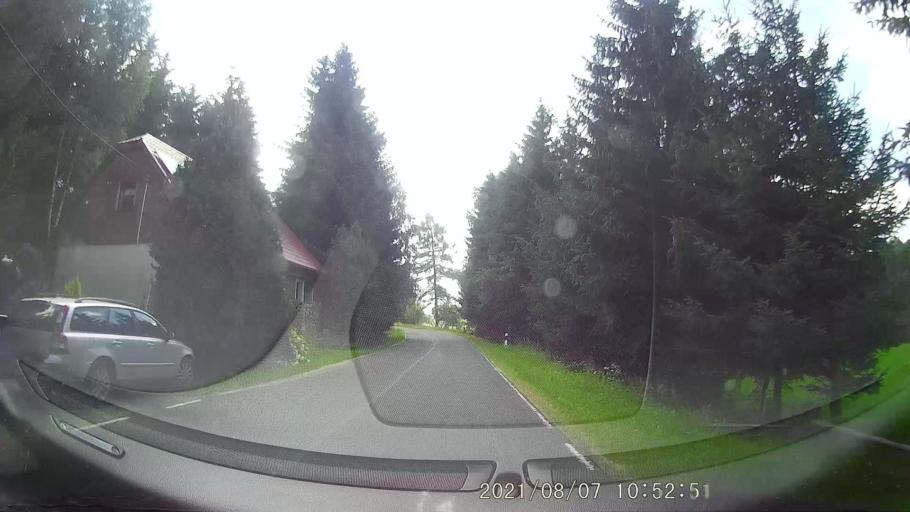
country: CZ
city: Rokytnice v Orlickych Horach
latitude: 50.2795
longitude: 16.4775
